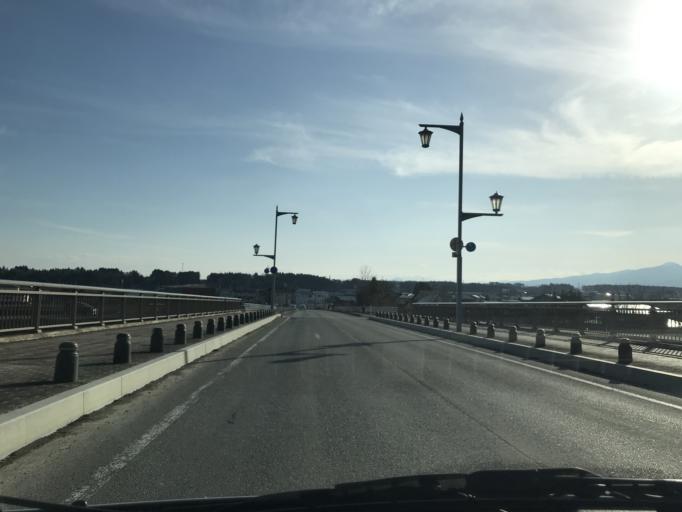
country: JP
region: Iwate
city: Kitakami
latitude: 39.2768
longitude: 141.1074
